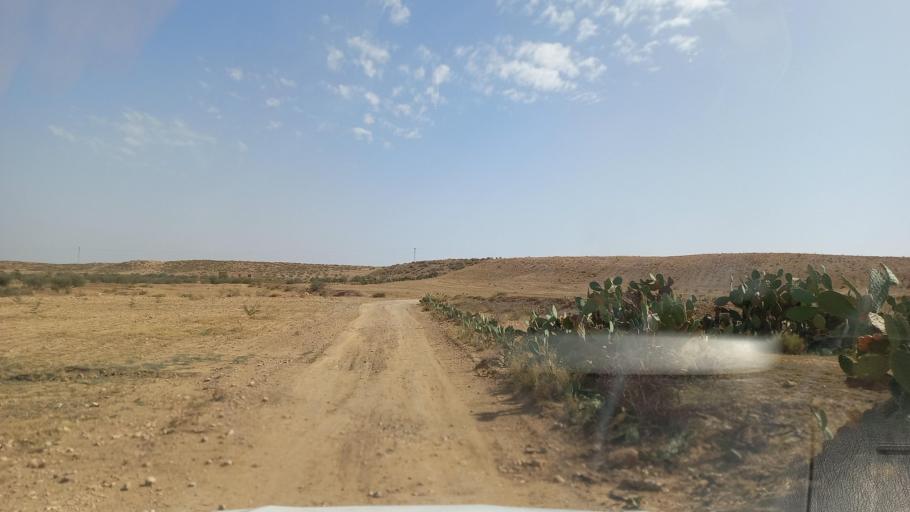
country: TN
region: Al Qasrayn
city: Kasserine
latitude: 35.2720
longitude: 8.9561
